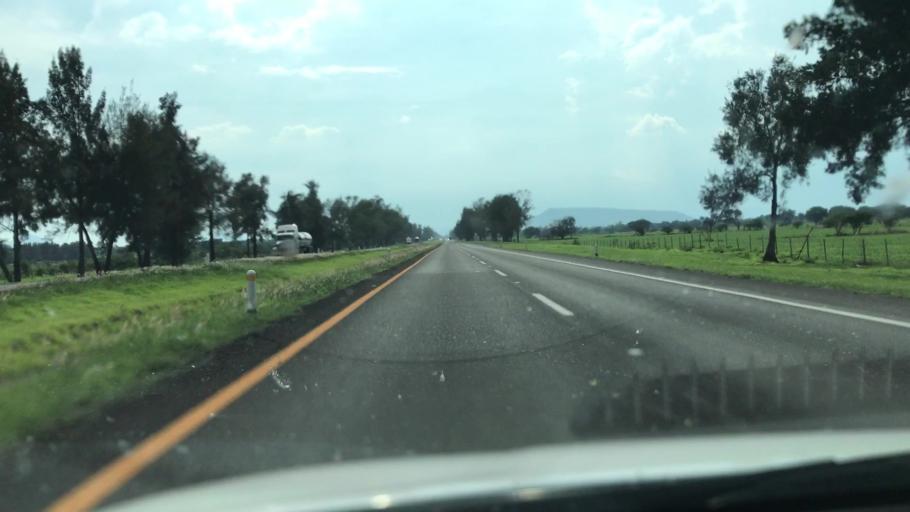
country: MX
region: Jalisco
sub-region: Ocotlan
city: Joconoxtle (La Tuna)
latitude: 20.3761
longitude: -102.6727
